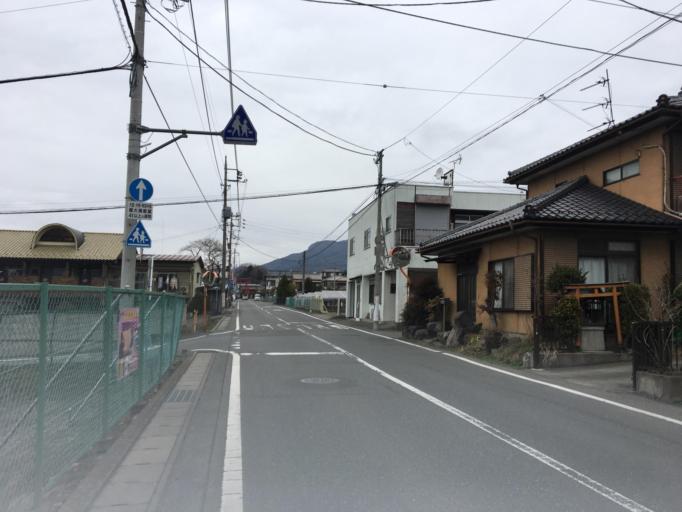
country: JP
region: Gunma
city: Numata
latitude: 36.6447
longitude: 139.0373
